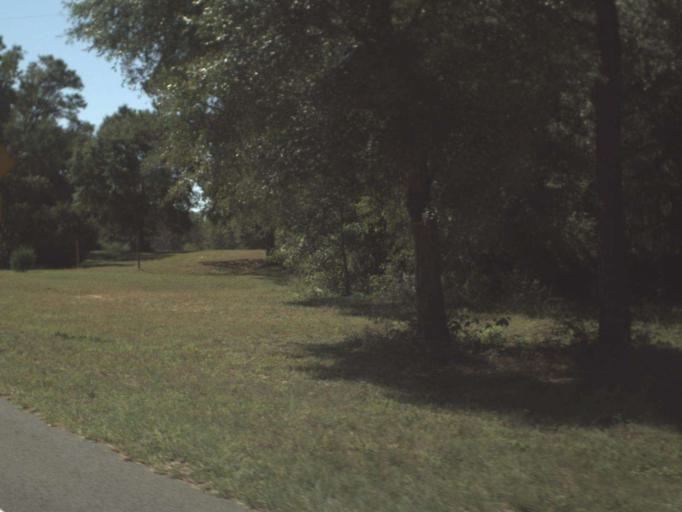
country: US
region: Alabama
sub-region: Covington County
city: Florala
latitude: 30.9708
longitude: -86.3542
